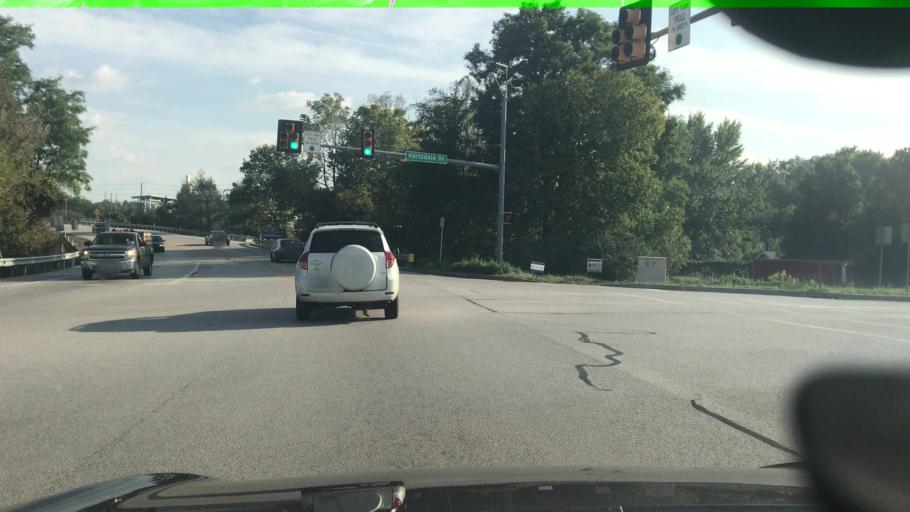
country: US
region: Pennsylvania
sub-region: Cumberland County
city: Shiremanstown
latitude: 40.2120
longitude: -76.9450
